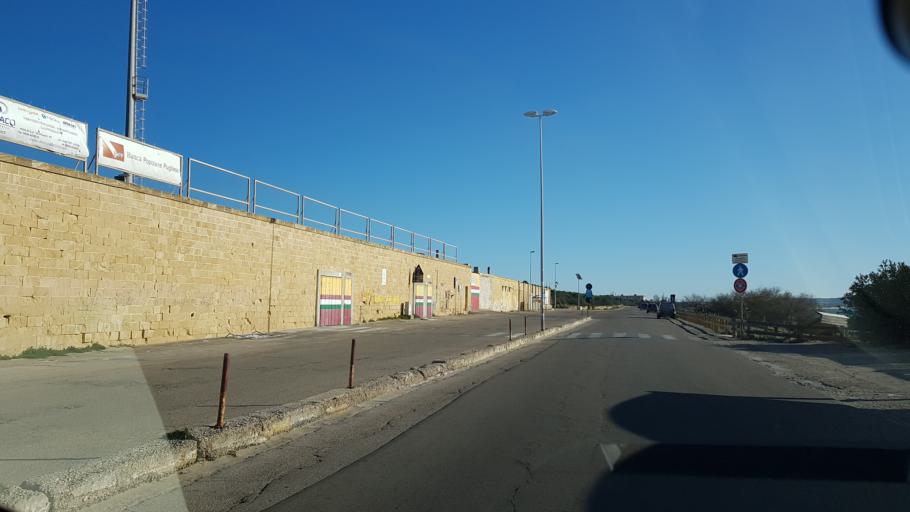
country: IT
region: Apulia
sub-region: Provincia di Lecce
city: Gallipoli
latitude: 40.0461
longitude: 18.0066
